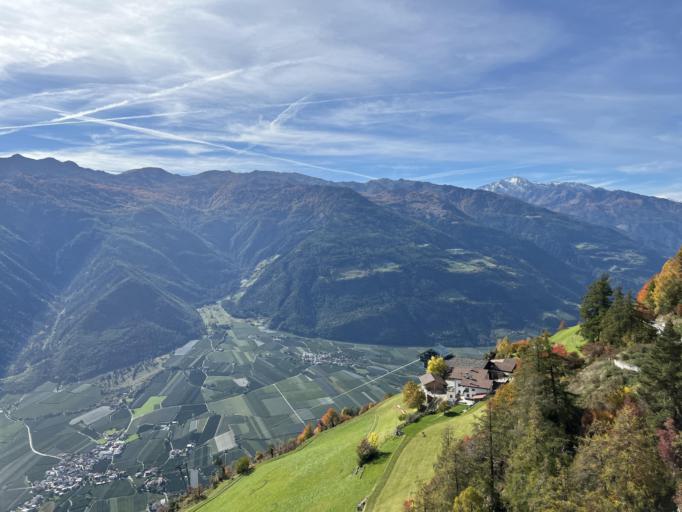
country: IT
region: Trentino-Alto Adige
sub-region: Bolzano
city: Naturno
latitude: 46.6606
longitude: 10.9848
